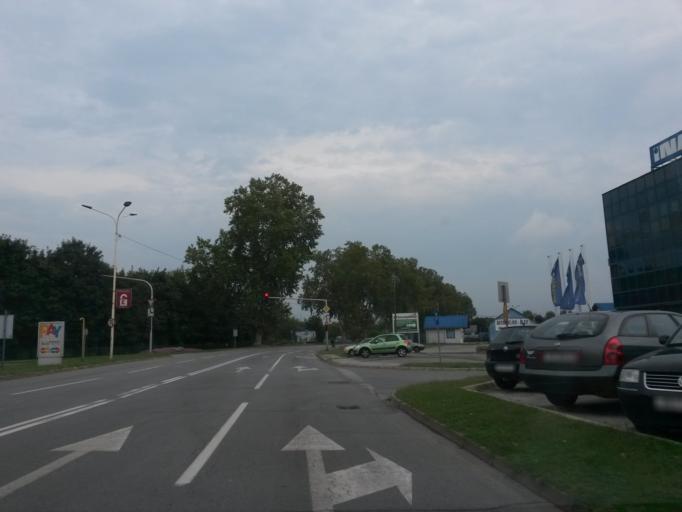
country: HR
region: Osjecko-Baranjska
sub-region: Grad Osijek
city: Osijek
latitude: 45.5511
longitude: 18.7323
